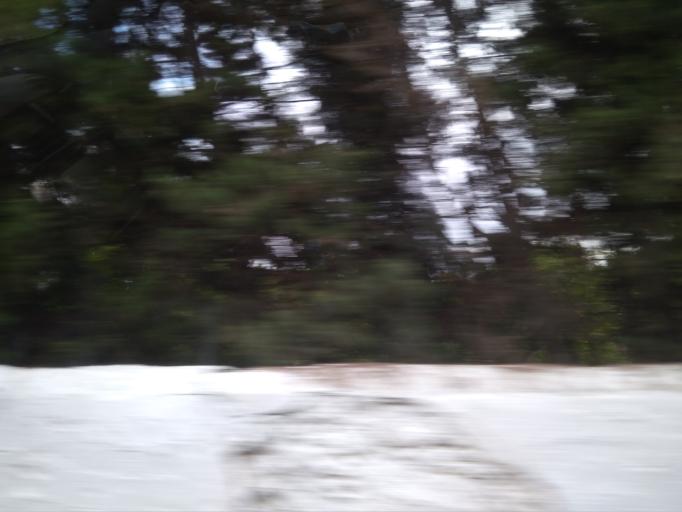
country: PT
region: Faro
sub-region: Faro
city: Santa Barbara de Nexe
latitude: 37.0661
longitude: -7.9557
